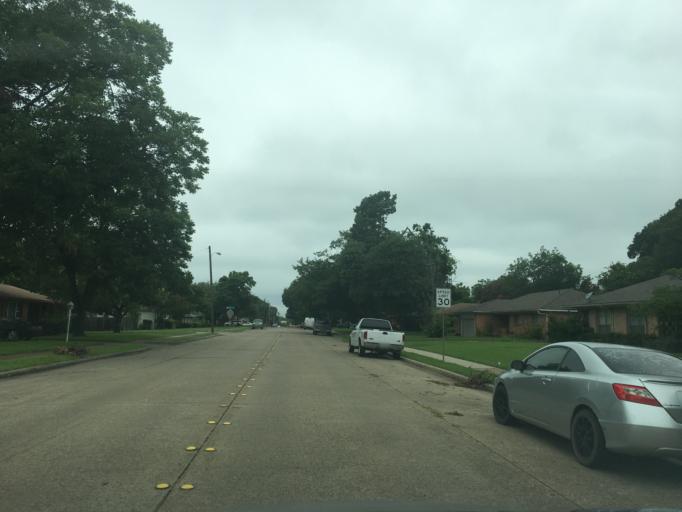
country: US
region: Texas
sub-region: Dallas County
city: Richardson
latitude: 32.9474
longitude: -96.7234
